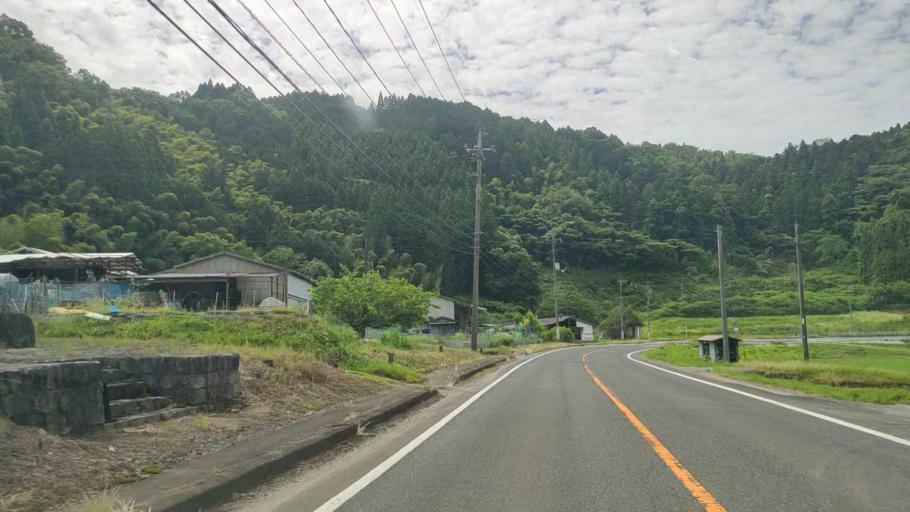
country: JP
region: Okayama
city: Niimi
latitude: 35.0926
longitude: 133.6535
